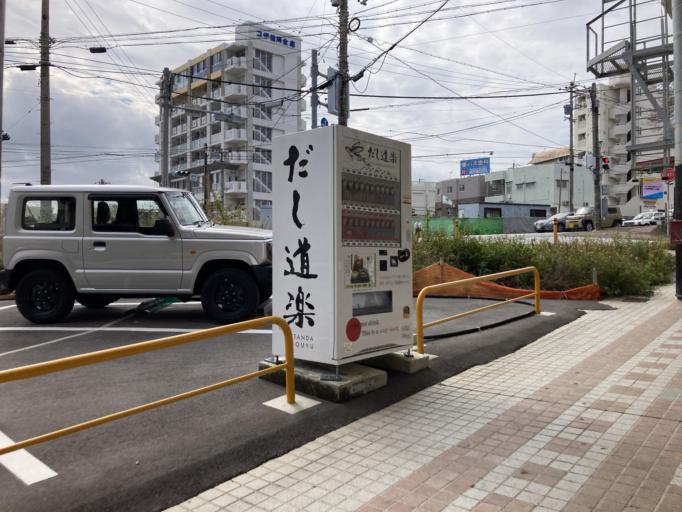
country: JP
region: Okinawa
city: Naha-shi
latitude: 26.2118
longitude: 127.6882
